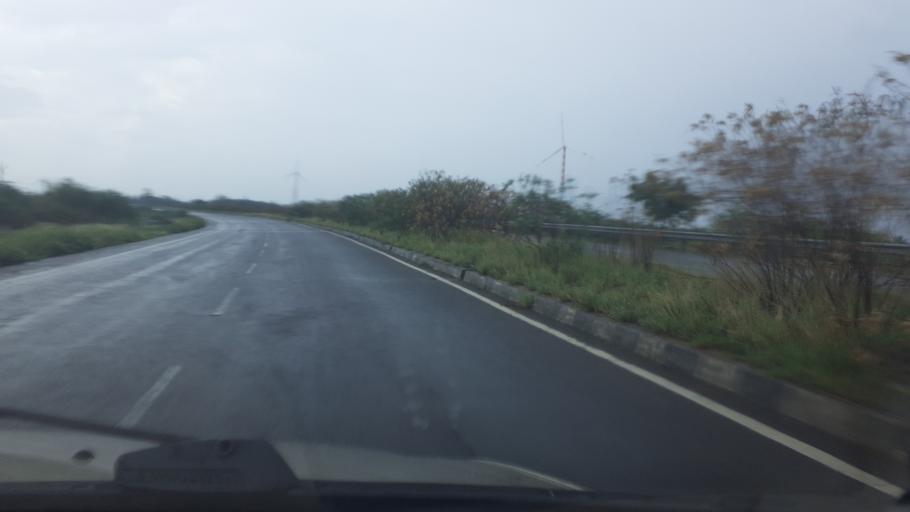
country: IN
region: Tamil Nadu
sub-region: Thoothukkudi
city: Kayattar
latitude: 8.9913
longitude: 77.7784
